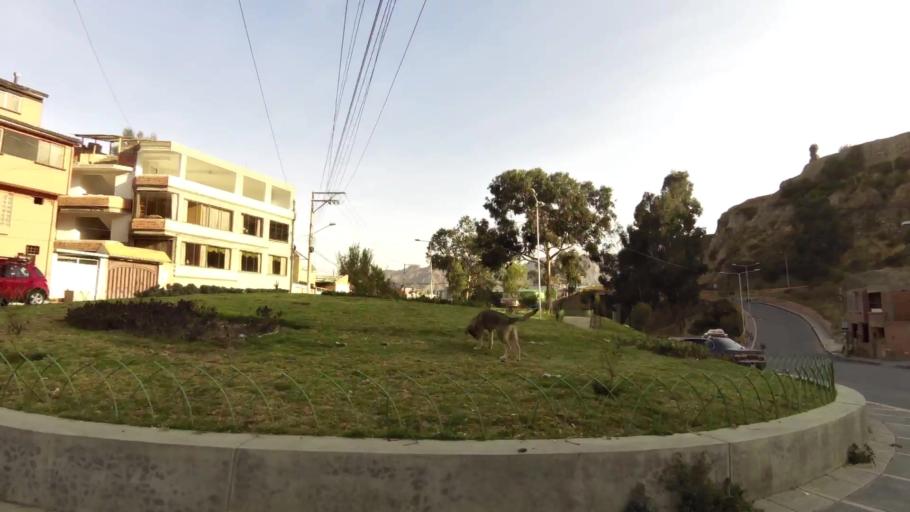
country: BO
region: La Paz
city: La Paz
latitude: -16.5240
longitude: -68.0996
